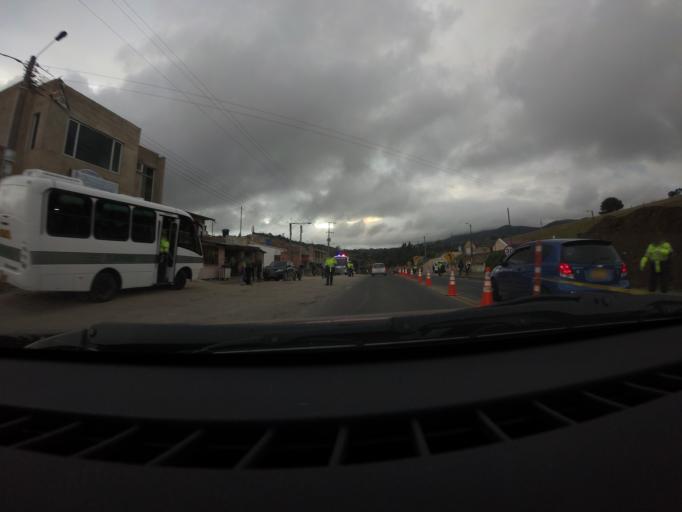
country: CO
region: Boyaca
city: Samaca
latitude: 5.4467
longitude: -73.4340
